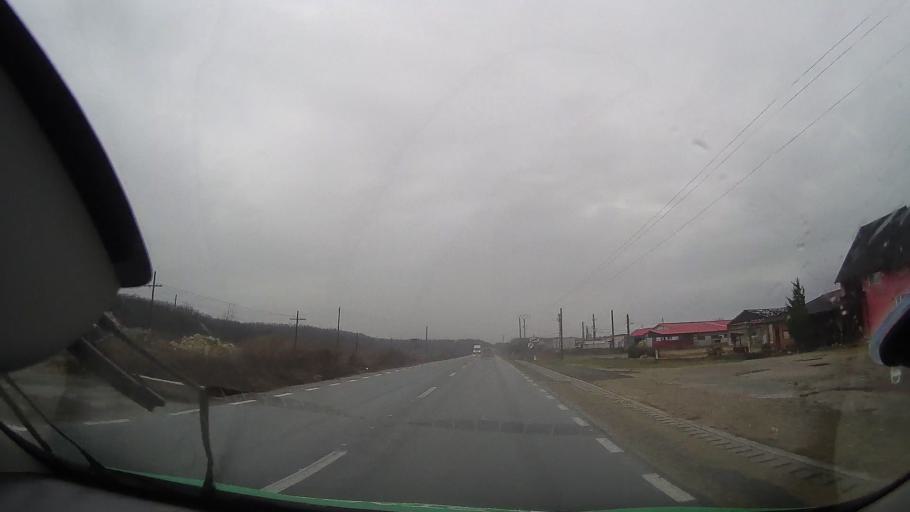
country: RO
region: Bihor
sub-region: Comuna Olcea
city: Olcea
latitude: 46.6883
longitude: 21.9658
